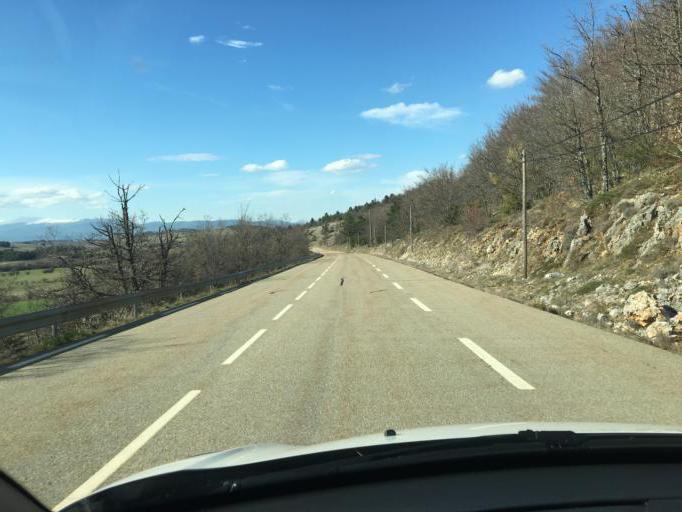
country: FR
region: Provence-Alpes-Cote d'Azur
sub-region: Departement du Vaucluse
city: Sault
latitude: 44.0111
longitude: 5.4757
